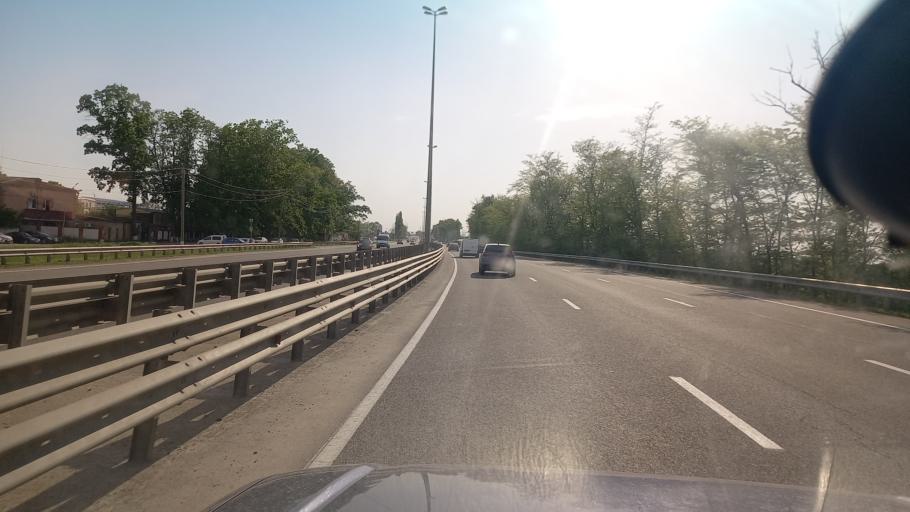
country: RU
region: Krasnodarskiy
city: Yelizavetinskaya
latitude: 45.0567
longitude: 38.8669
